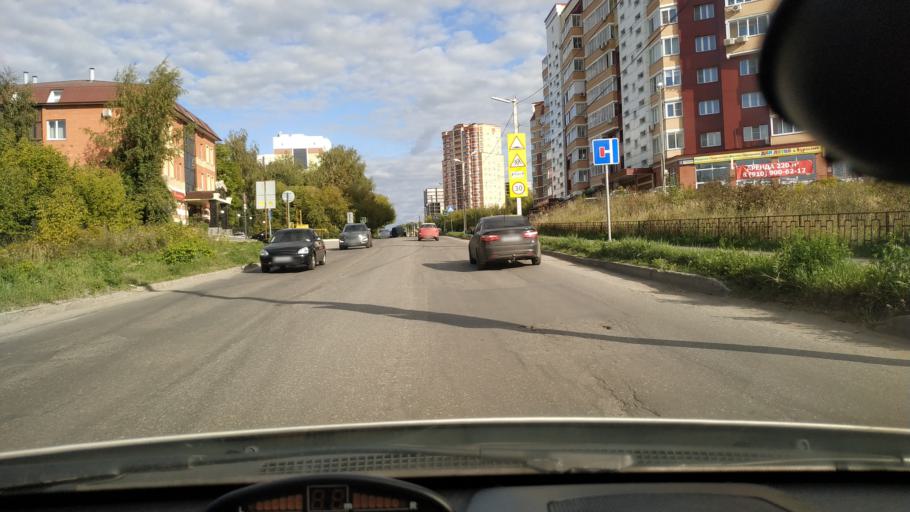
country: RU
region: Rjazan
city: Ryazan'
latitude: 54.6056
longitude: 39.7335
